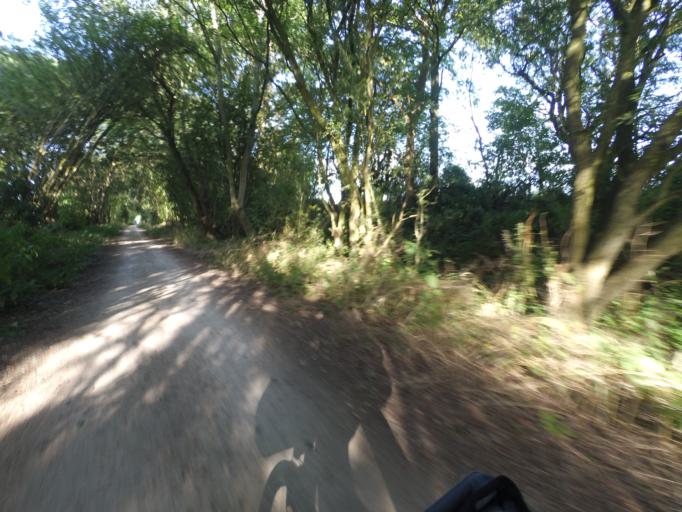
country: GB
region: England
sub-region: Staffordshire
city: Stafford
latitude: 52.7988
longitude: -2.1784
